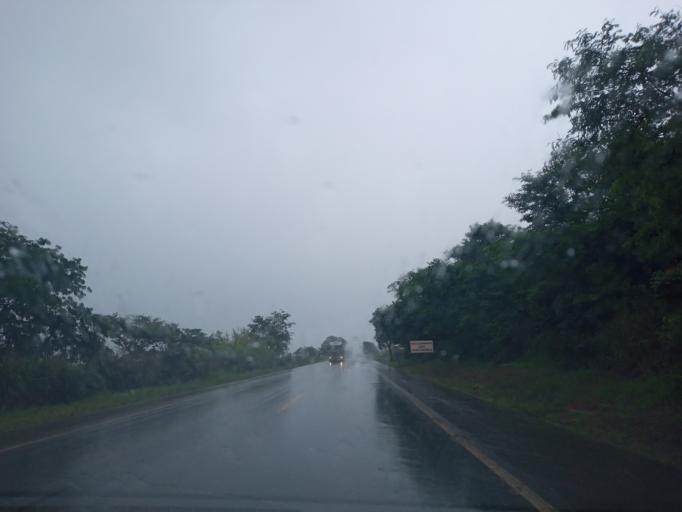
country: BR
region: Minas Gerais
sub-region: Luz
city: Luz
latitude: -19.7844
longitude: -45.7084
